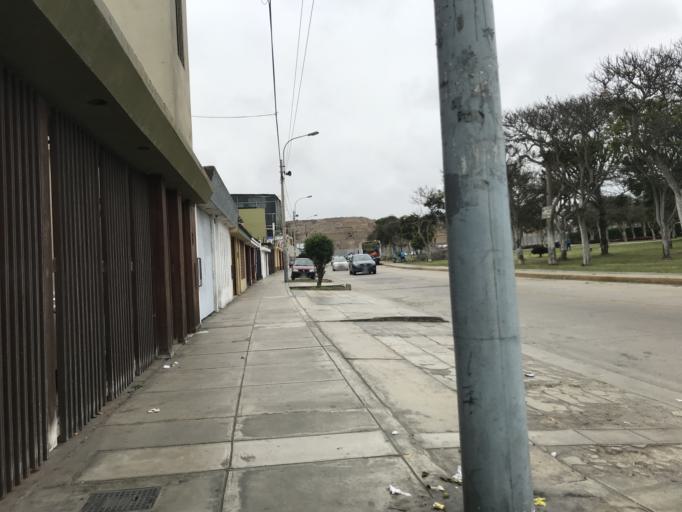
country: PE
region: Callao
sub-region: Callao
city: Callao
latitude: -12.0758
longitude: -77.0852
